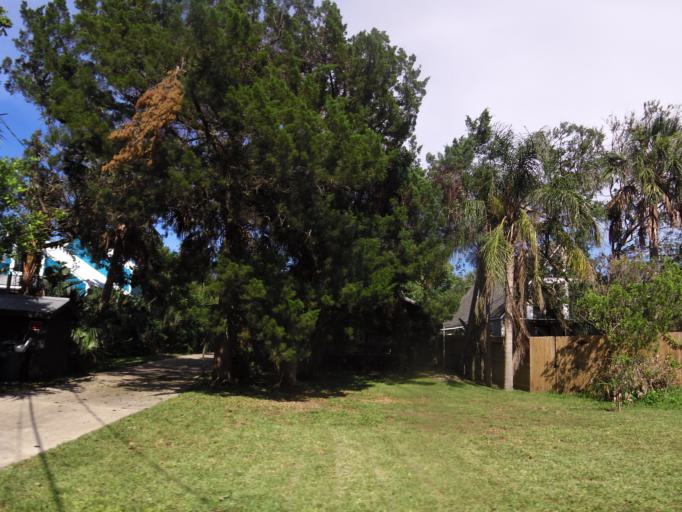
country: US
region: Florida
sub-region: Saint Johns County
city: Villano Beach
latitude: 29.9152
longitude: -81.2965
